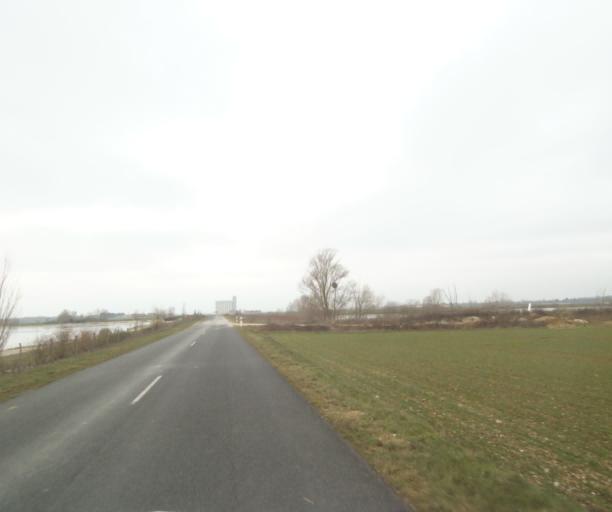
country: FR
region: Champagne-Ardenne
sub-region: Departement de la Haute-Marne
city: Villiers-en-Lieu
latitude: 48.6532
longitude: 4.7778
